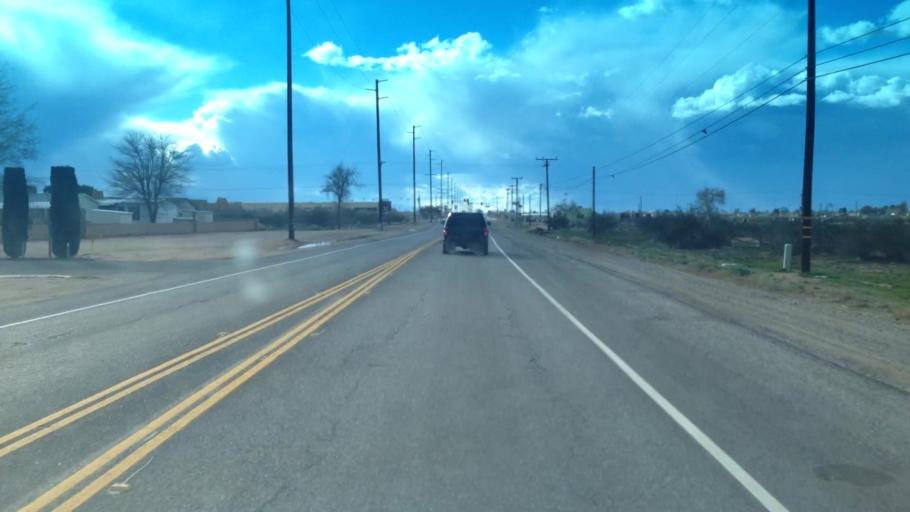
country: US
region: California
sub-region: San Bernardino County
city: Apple Valley
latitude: 34.4717
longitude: -117.1690
